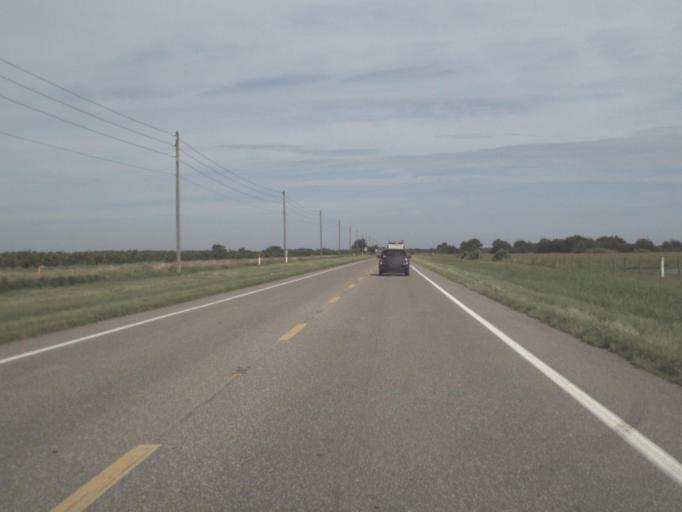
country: US
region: Florida
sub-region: DeSoto County
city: Nocatee
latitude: 27.0290
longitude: -81.7682
